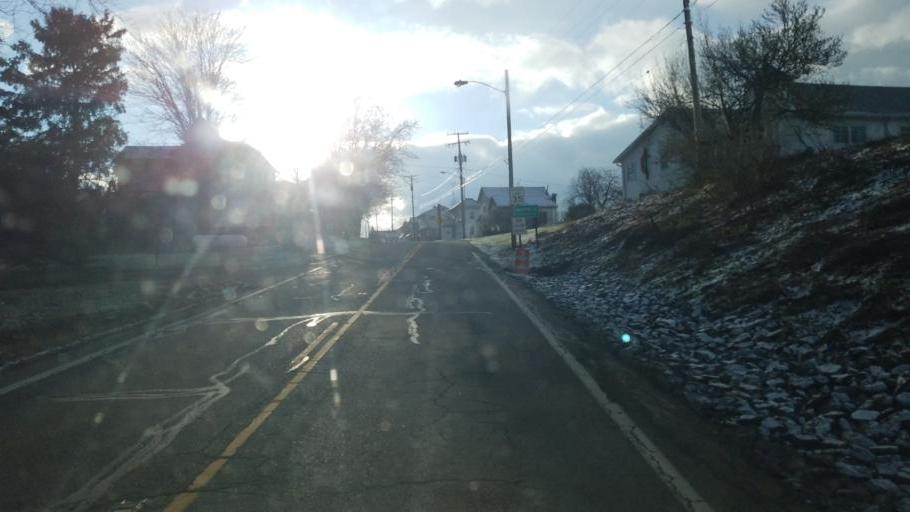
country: US
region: Ohio
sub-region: Ashland County
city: Loudonville
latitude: 40.5976
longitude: -82.1163
